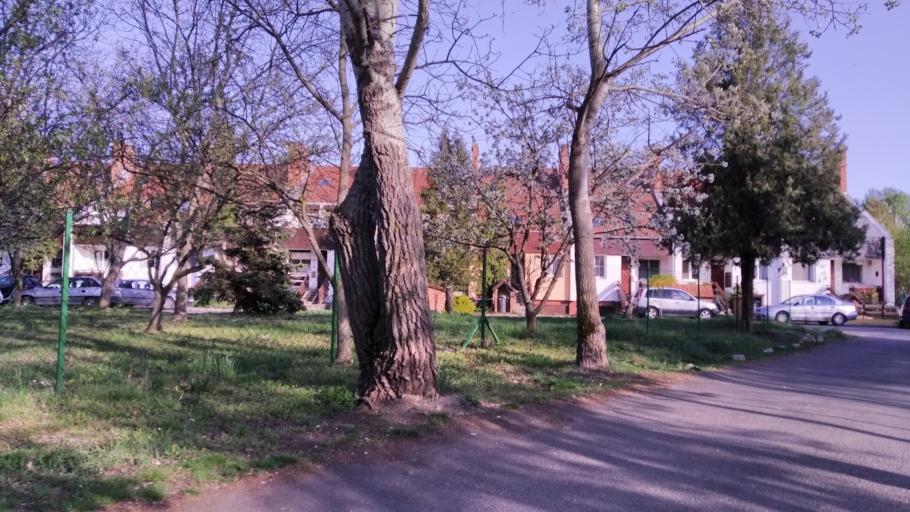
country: HU
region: Pest
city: Budakalasz
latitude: 47.6251
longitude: 19.0497
